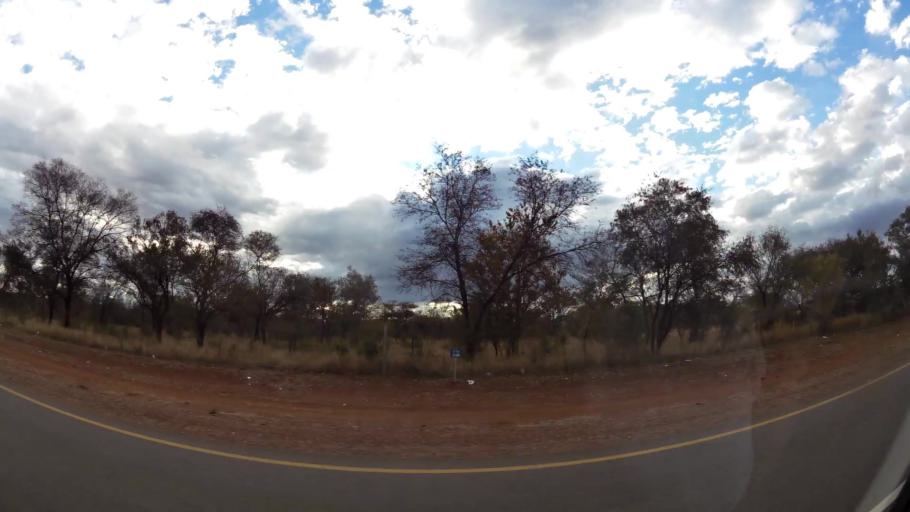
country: ZA
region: Limpopo
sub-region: Waterberg District Municipality
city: Modimolle
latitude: -24.5036
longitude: 28.7300
